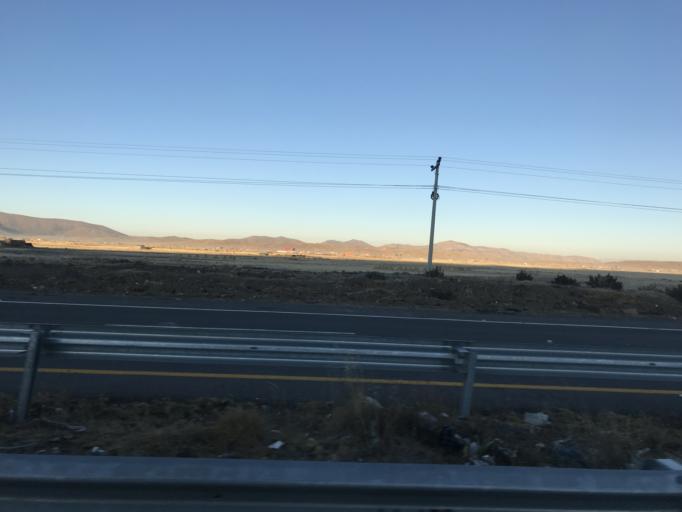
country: BO
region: La Paz
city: Batallas
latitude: -16.2904
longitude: -68.5415
